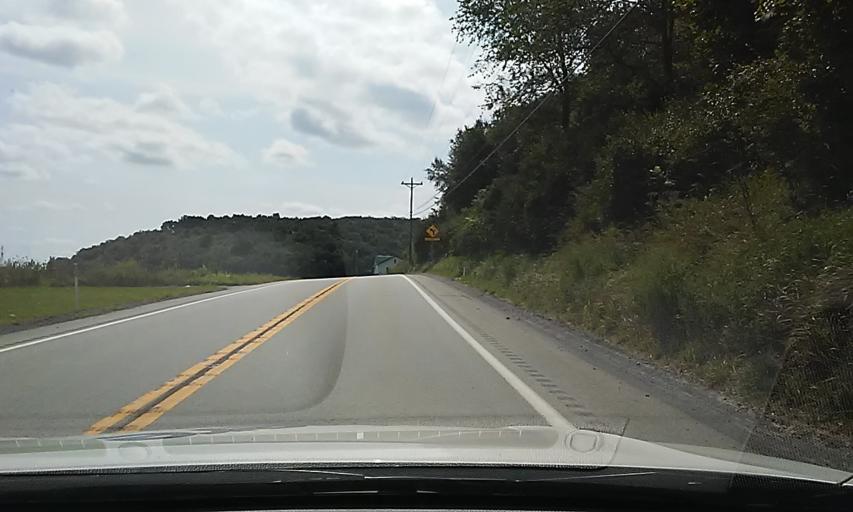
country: US
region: Pennsylvania
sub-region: Jefferson County
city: Punxsutawney
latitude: 40.8178
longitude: -79.0510
